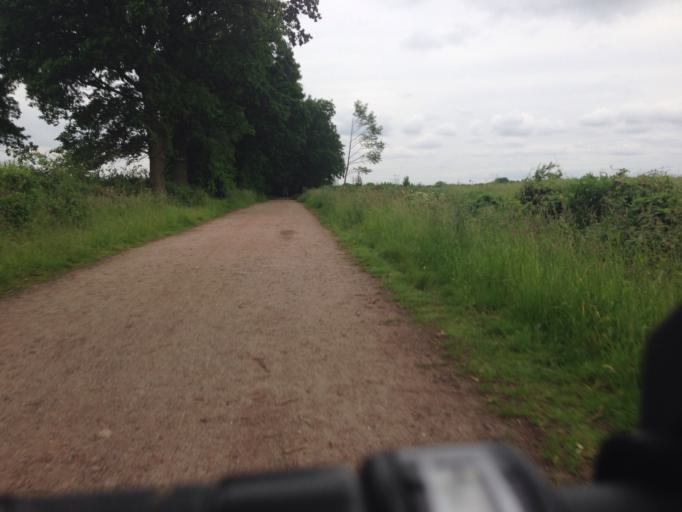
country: DE
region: Schleswig-Holstein
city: Barsbuettel
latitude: 53.5816
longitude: 10.1654
